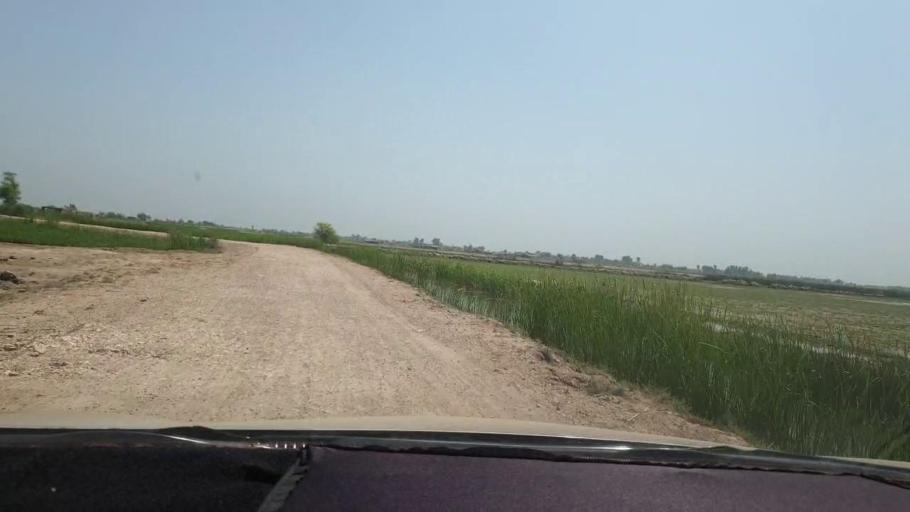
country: PK
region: Sindh
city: Shahdadkot
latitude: 27.8252
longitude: 67.9919
